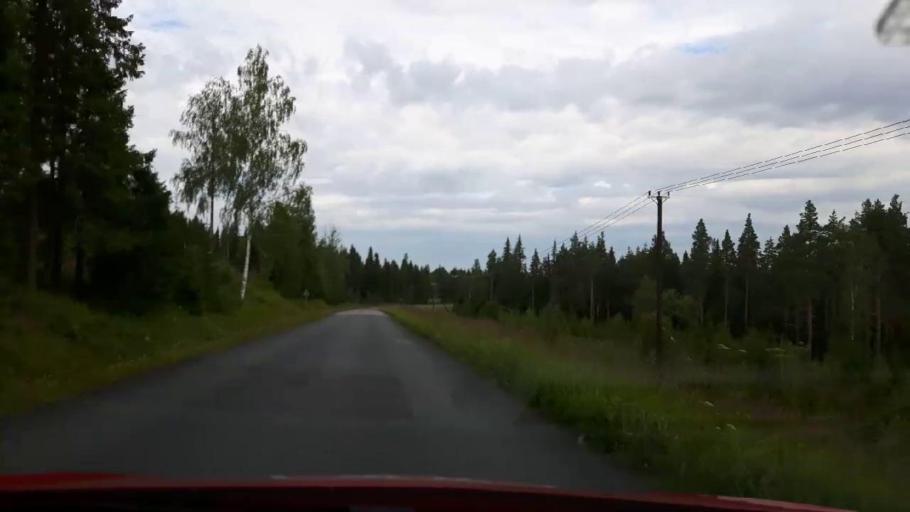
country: SE
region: Jaemtland
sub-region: Stroemsunds Kommun
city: Stroemsund
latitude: 63.5307
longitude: 15.3562
